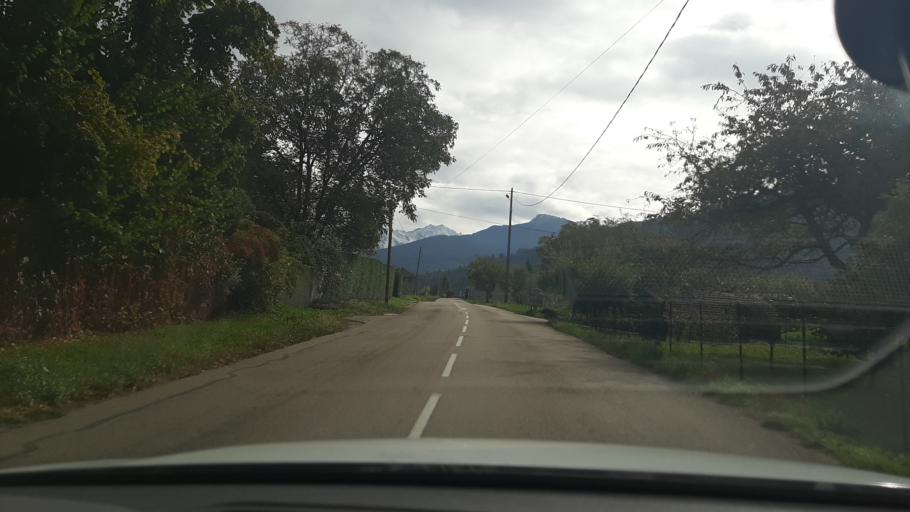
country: FR
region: Rhone-Alpes
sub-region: Departement de la Savoie
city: Montmelian
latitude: 45.4506
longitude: 6.0629
